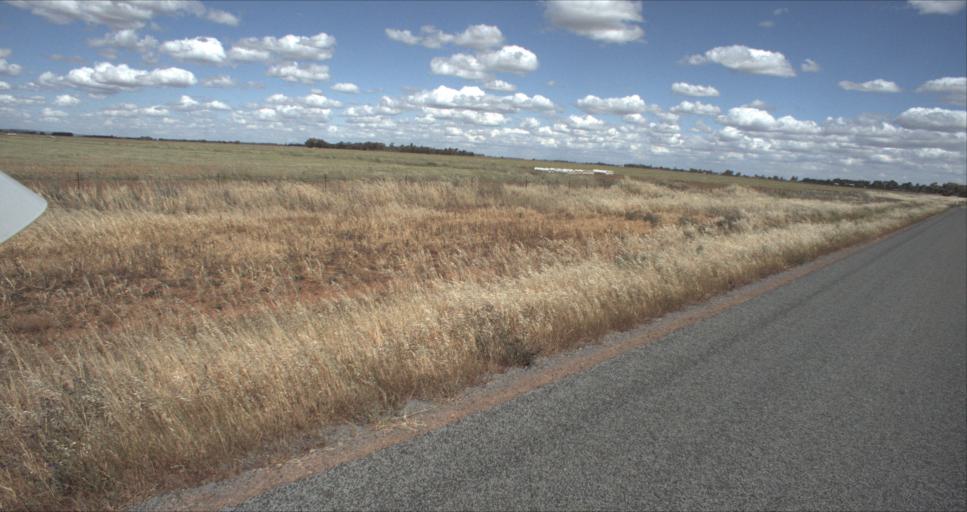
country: AU
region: New South Wales
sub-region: Leeton
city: Leeton
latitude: -34.4642
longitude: 146.2522
